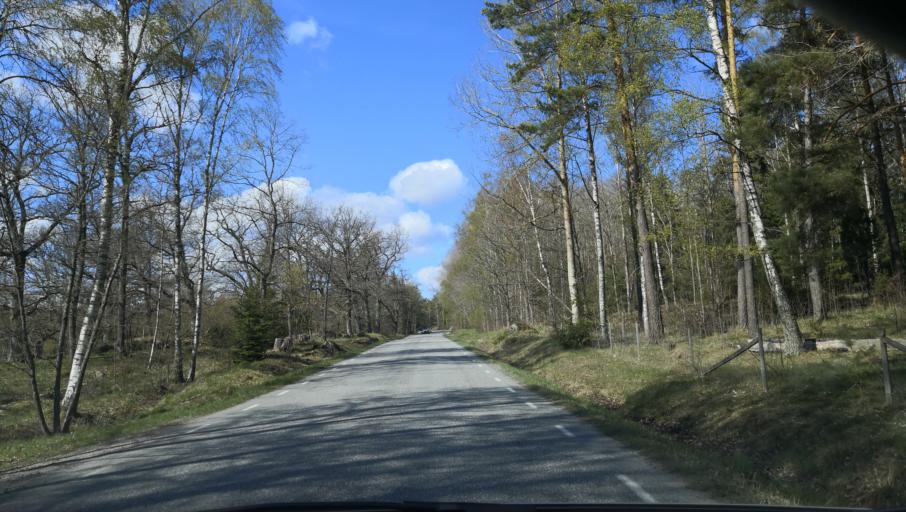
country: SE
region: Stockholm
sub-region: Varmdo Kommun
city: Hemmesta
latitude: 59.3939
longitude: 18.5125
